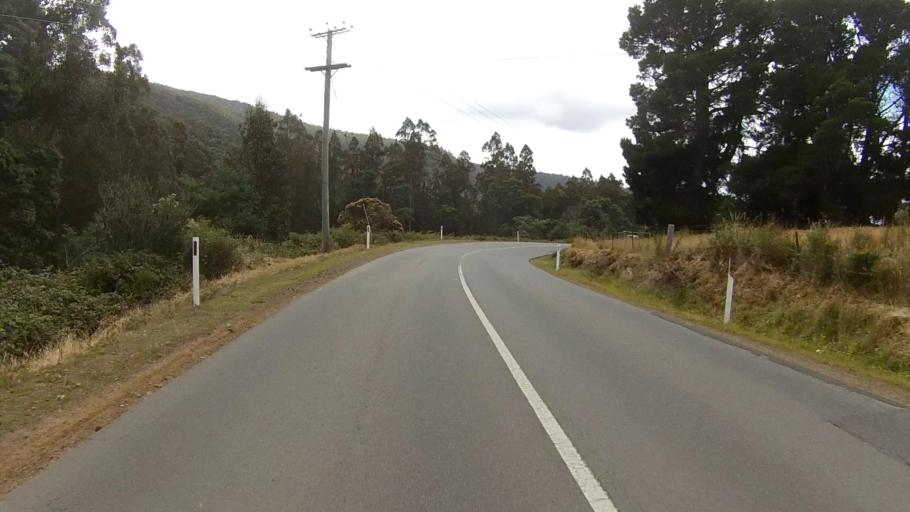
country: AU
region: Tasmania
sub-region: Kingborough
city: Kettering
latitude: -43.1127
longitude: 147.1946
